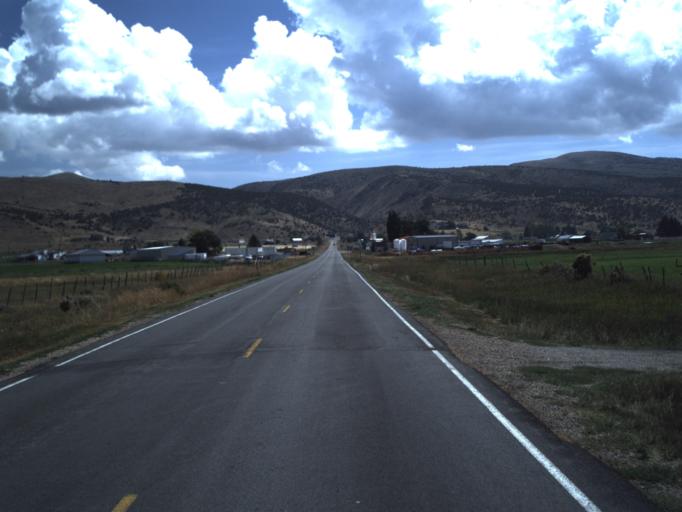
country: US
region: Utah
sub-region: Rich County
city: Randolph
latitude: 41.8340
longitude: -111.3283
